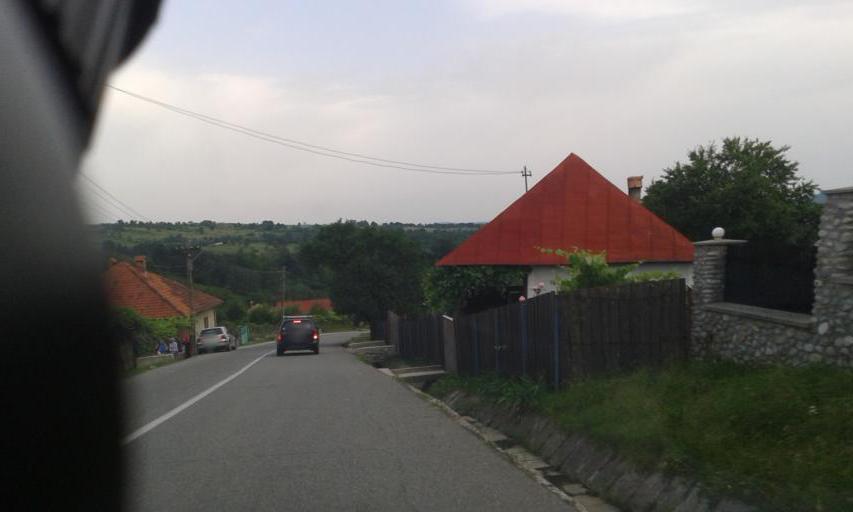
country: RO
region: Gorj
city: Novaci-Straini
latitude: 45.1832
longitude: 23.6817
